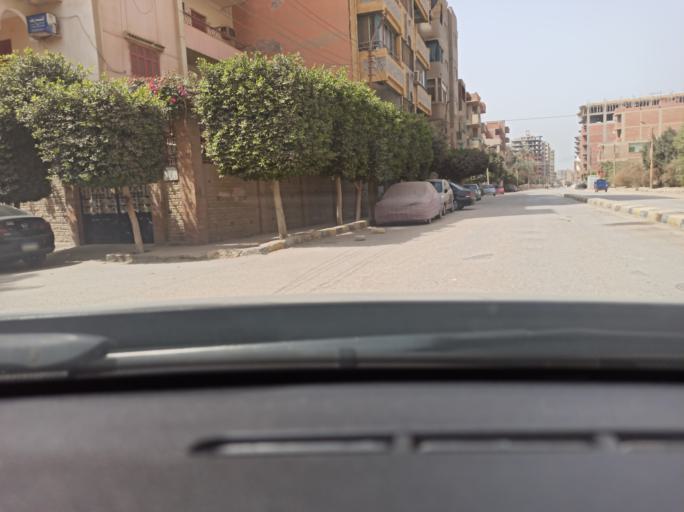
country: EG
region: Muhafazat Bani Suwayf
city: Bani Suwayf
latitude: 29.0829
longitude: 31.0887
